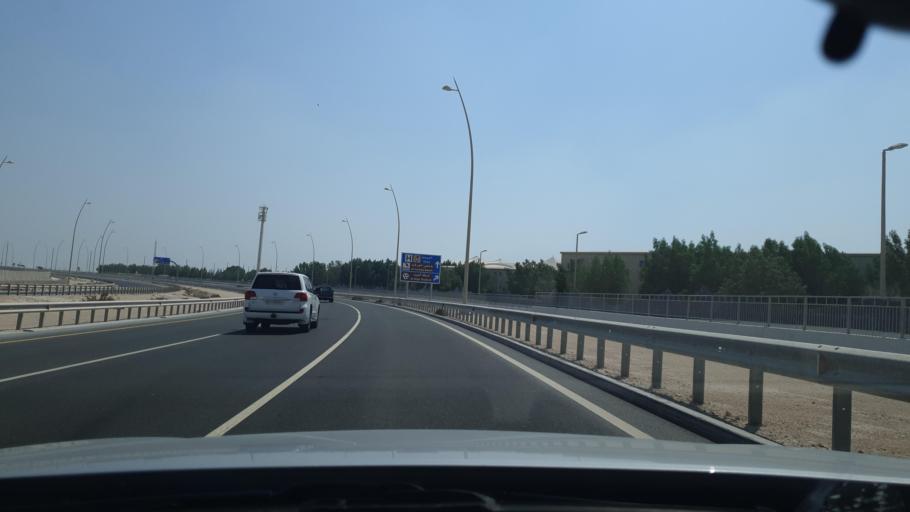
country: QA
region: Al Khawr
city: Al Khawr
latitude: 25.6614
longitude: 51.4796
